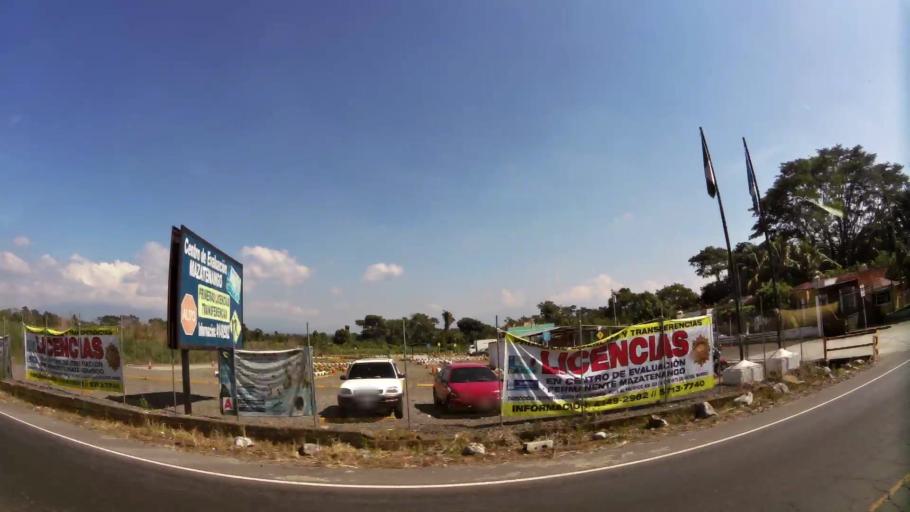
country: GT
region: Suchitepeque
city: Mazatenango
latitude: 14.5479
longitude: -91.5052
